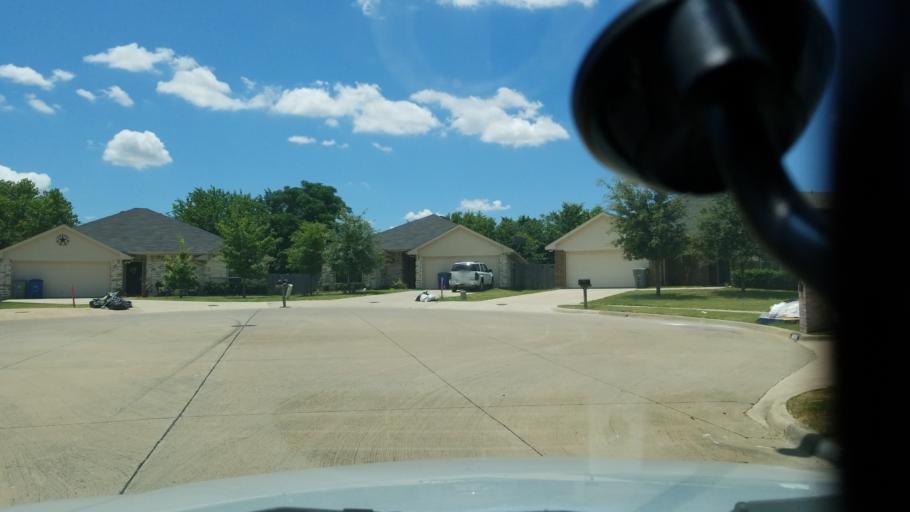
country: US
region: Texas
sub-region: Dallas County
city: Duncanville
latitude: 32.6662
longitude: -96.8791
